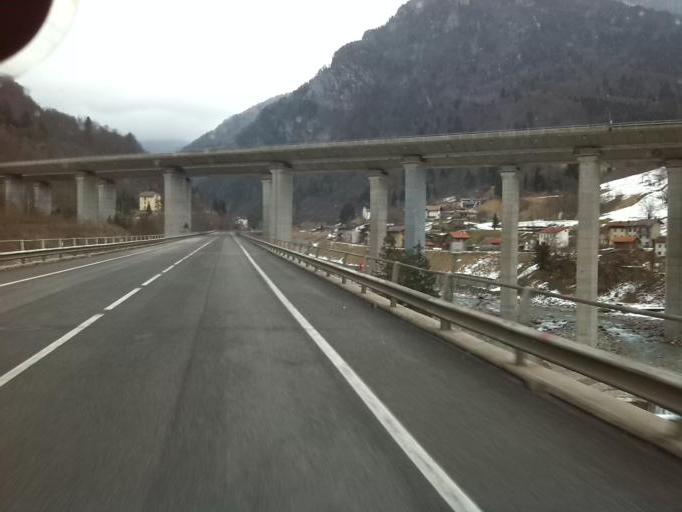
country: IT
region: Friuli Venezia Giulia
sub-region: Provincia di Udine
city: Pontebba
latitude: 46.4749
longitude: 13.2943
